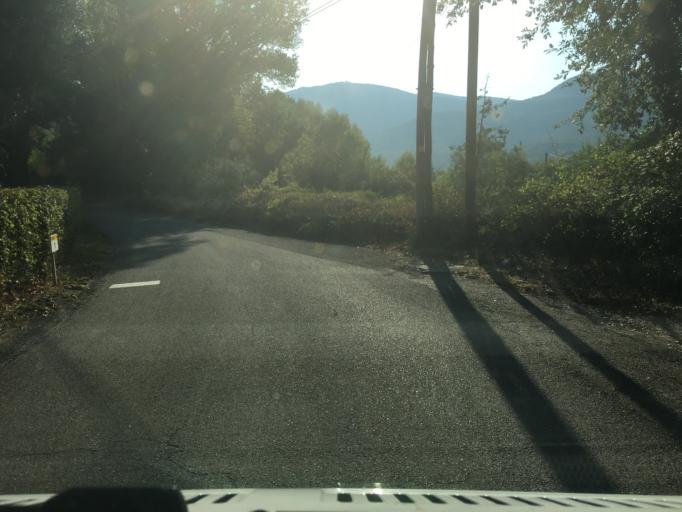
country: FR
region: Provence-Alpes-Cote d'Azur
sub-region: Departement des Alpes-de-Haute-Provence
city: Mallemoisson
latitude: 43.9408
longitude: 6.1805
